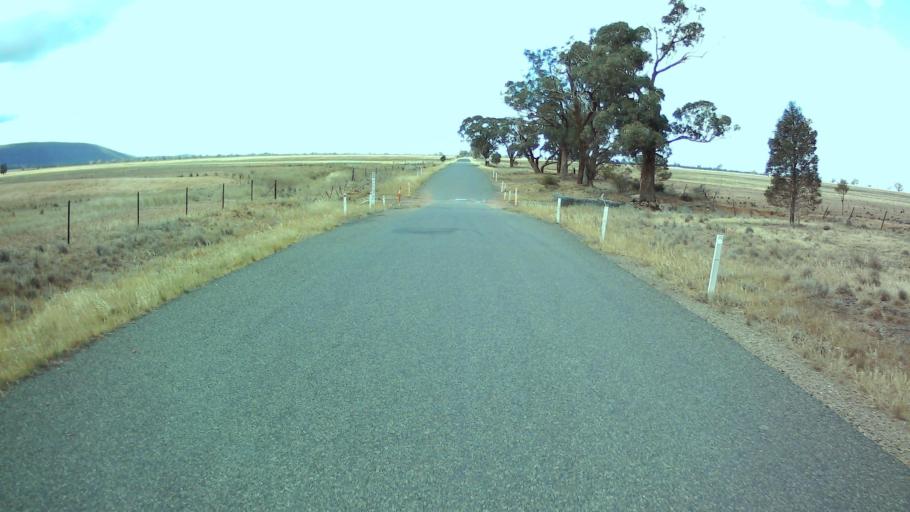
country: AU
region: New South Wales
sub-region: Weddin
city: Grenfell
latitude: -33.8663
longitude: 147.9272
